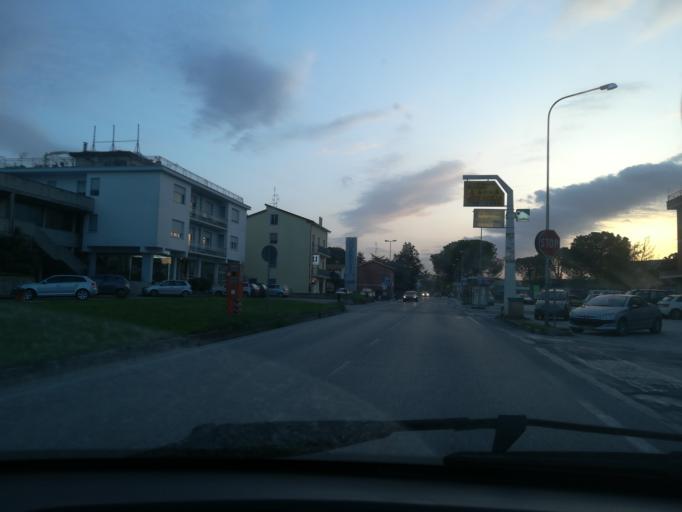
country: IT
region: The Marches
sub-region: Provincia di Macerata
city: Piediripa
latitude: 43.2757
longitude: 13.5025
